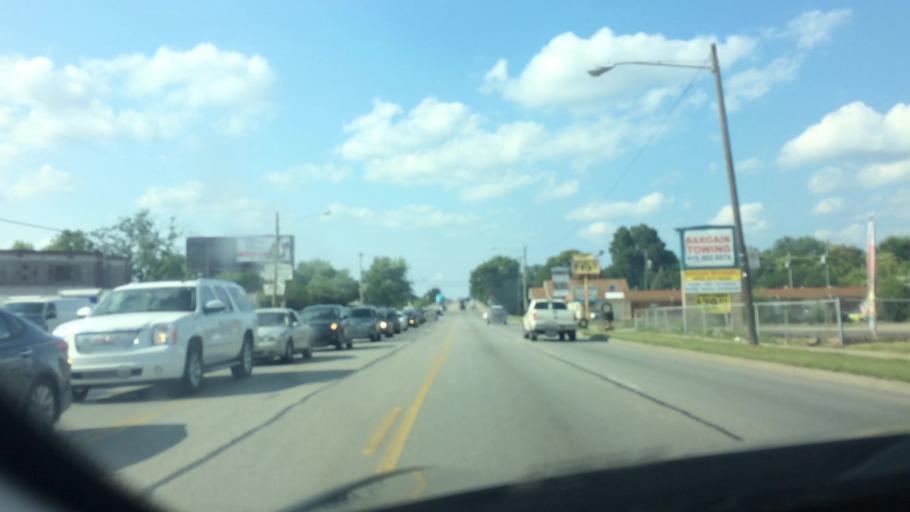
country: US
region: Ohio
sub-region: Lucas County
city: Ottawa Hills
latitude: 41.6259
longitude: -83.6258
